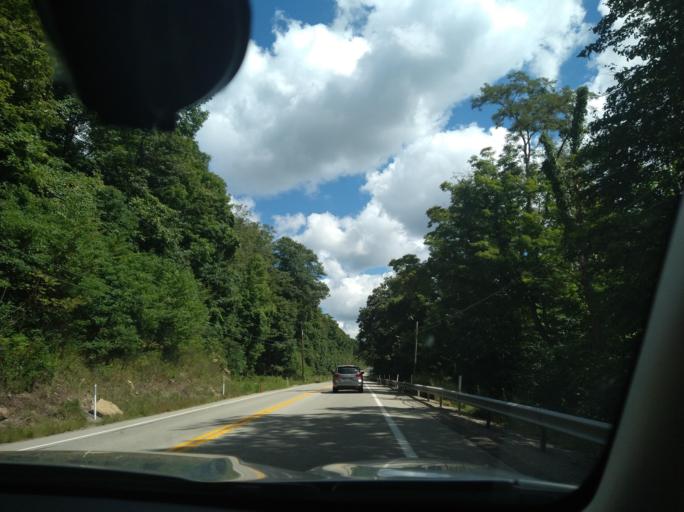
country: US
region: Pennsylvania
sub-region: Fayette County
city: Bear Rocks
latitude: 40.0742
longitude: -79.3083
